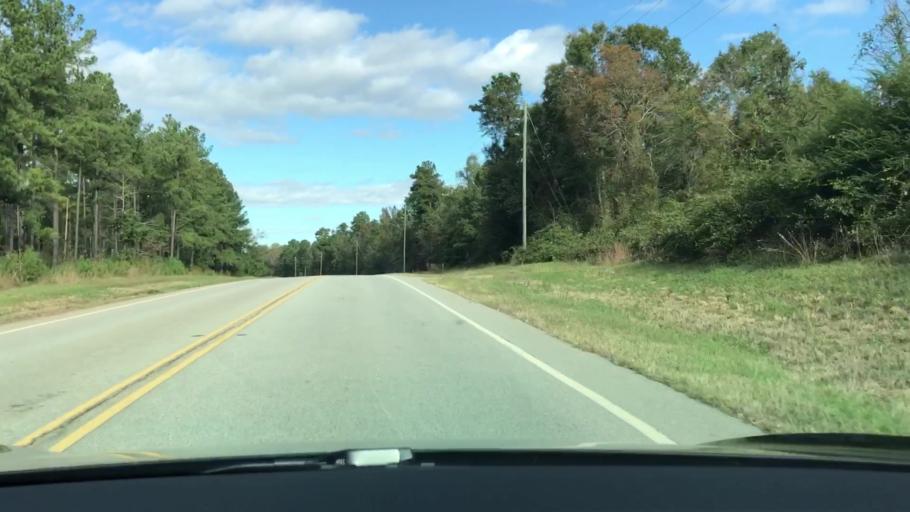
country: US
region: Georgia
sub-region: Jefferson County
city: Louisville
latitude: 33.0878
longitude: -82.4149
